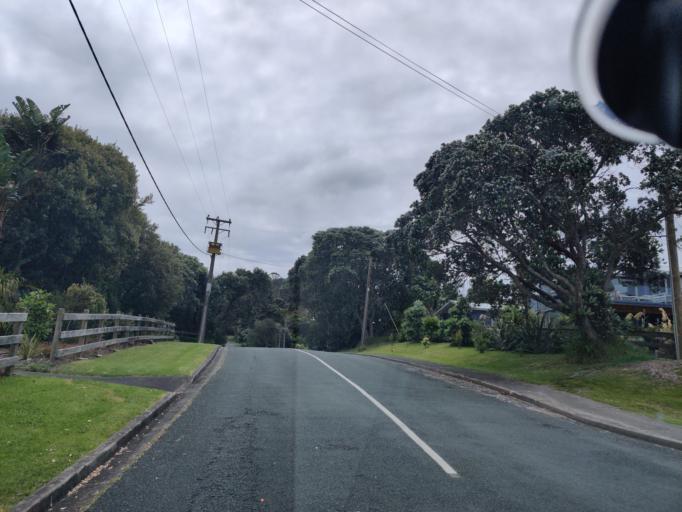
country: NZ
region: Auckland
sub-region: Auckland
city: Warkworth
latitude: -36.2981
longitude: 174.7984
